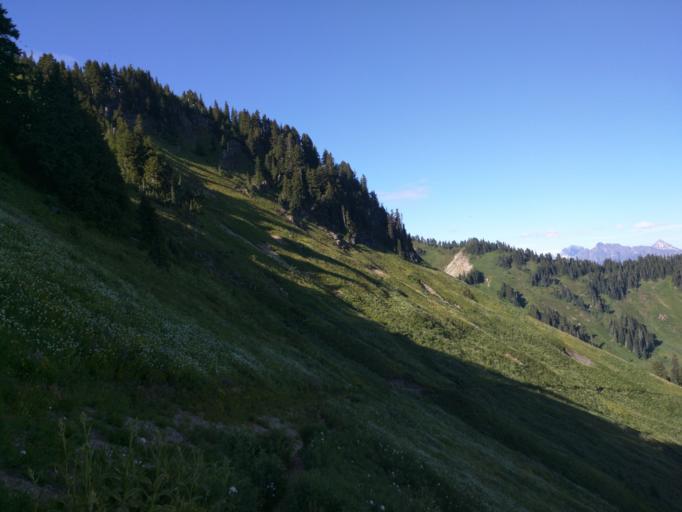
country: CA
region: British Columbia
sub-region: Fraser Valley Regional District
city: Chilliwack
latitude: 48.9250
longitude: -121.8735
